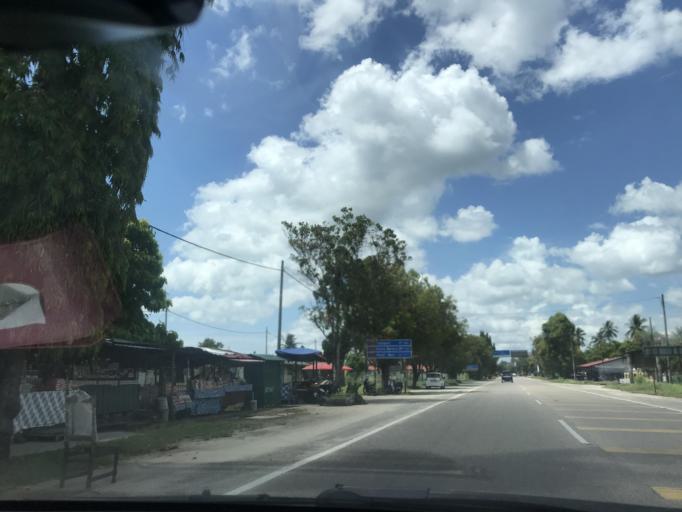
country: TH
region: Narathiwat
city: Tak Bai
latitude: 6.2307
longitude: 102.0924
